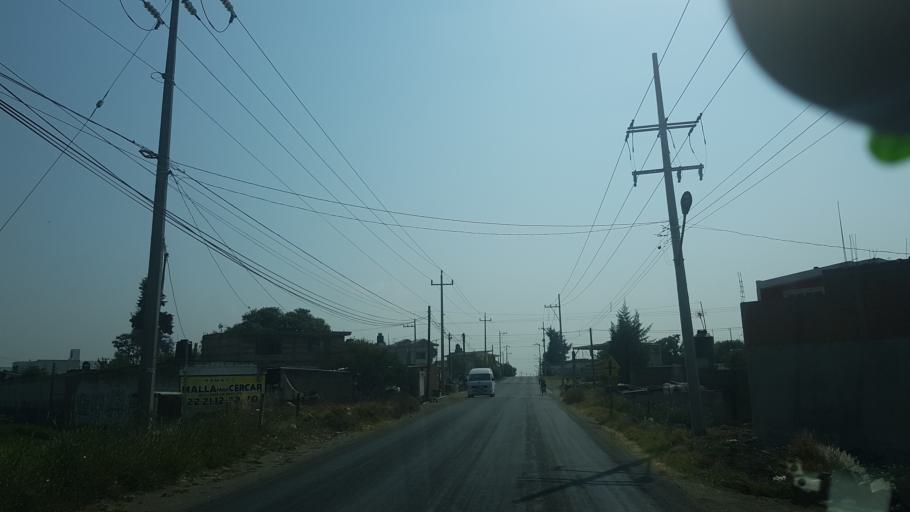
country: MX
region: Puebla
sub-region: San Jeronimo Tecuanipan
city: Los Reyes Tlanechicolpan
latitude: 19.0538
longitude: -98.3382
